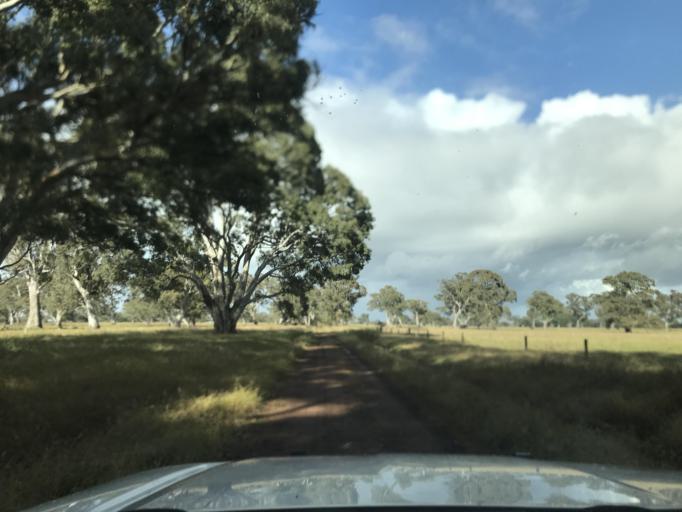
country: AU
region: South Australia
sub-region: Wattle Range
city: Penola
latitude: -37.1777
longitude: 141.3190
